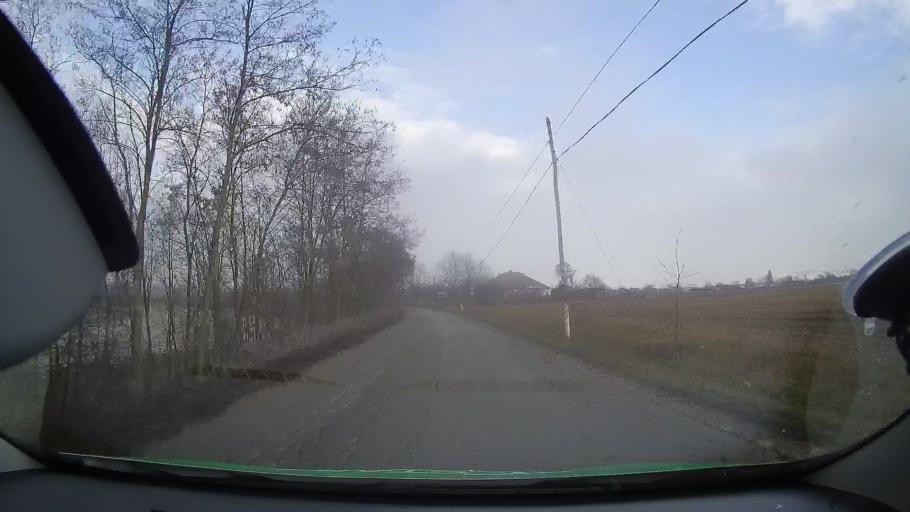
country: RO
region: Alba
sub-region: Comuna Noslac
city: Noslac
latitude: 46.4216
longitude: 23.9894
